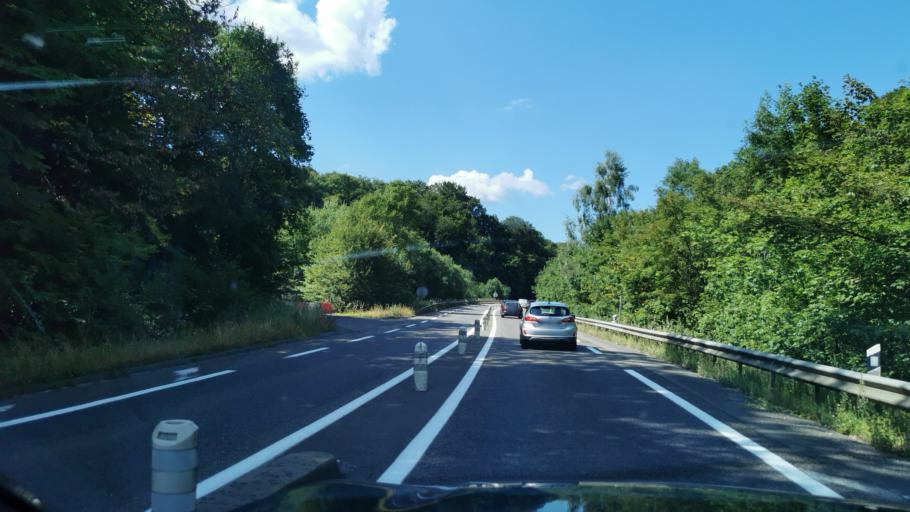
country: FR
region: Lorraine
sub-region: Departement de Meurthe-et-Moselle
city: Rehon
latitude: 49.5108
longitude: 5.7505
